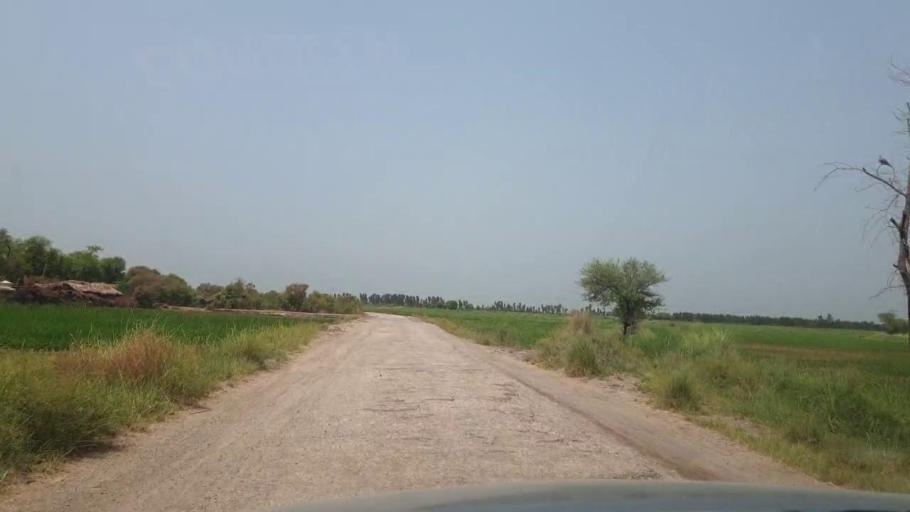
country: PK
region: Sindh
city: Garhi Yasin
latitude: 27.8842
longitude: 68.4390
